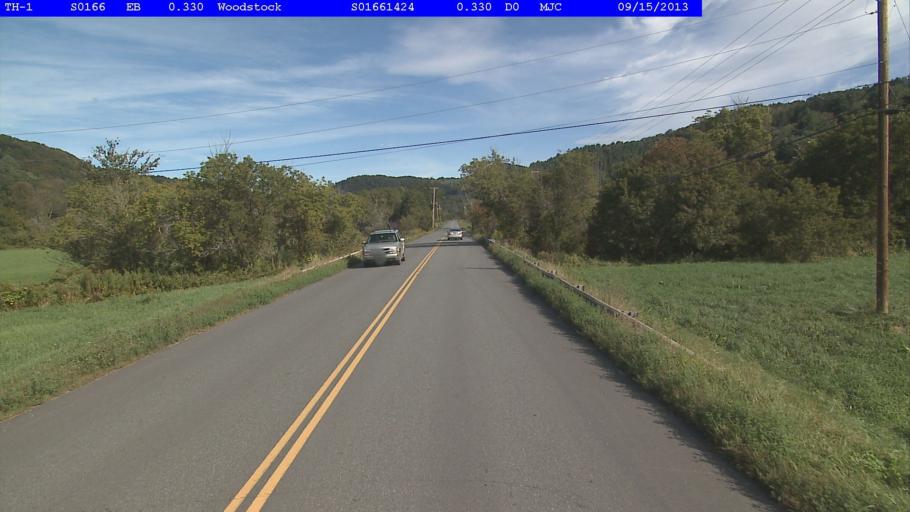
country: US
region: Vermont
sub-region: Windsor County
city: Woodstock
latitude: 43.6430
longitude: -72.5255
